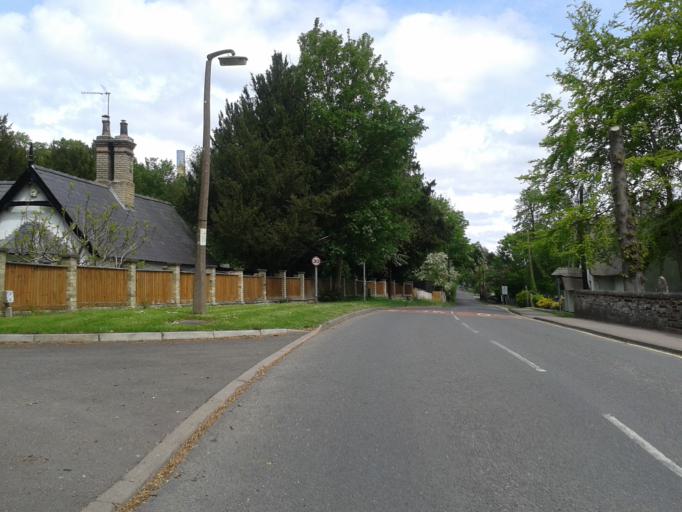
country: GB
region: England
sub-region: Cambridgeshire
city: Haslingfield
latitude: 52.1303
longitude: 0.0386
